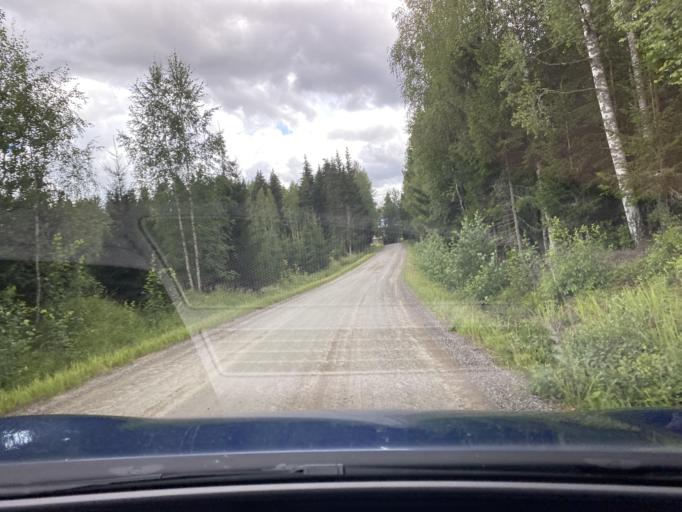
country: FI
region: Pirkanmaa
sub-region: Lounais-Pirkanmaa
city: Punkalaidun
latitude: 61.2194
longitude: 23.1653
